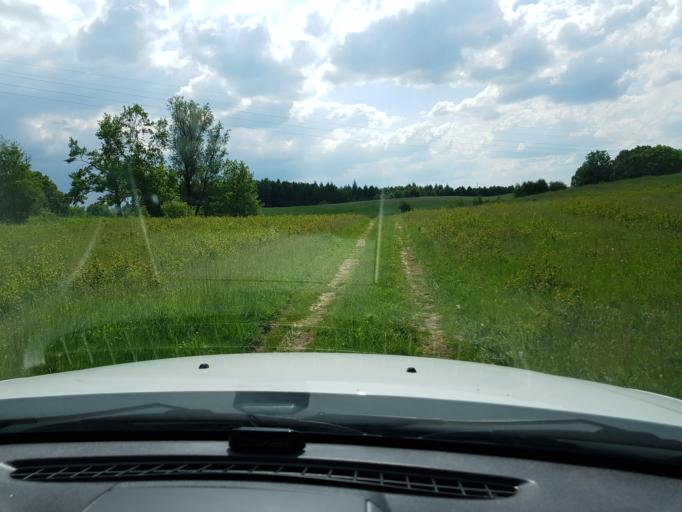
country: PL
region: West Pomeranian Voivodeship
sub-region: Powiat drawski
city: Drawsko Pomorskie
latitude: 53.5522
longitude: 15.7156
